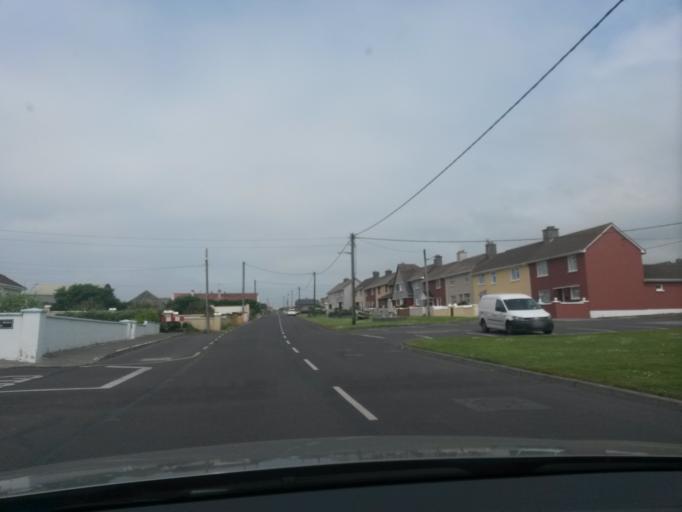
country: IE
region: Munster
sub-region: Ciarrai
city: Ballybunnion
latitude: 52.5193
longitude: -9.6735
